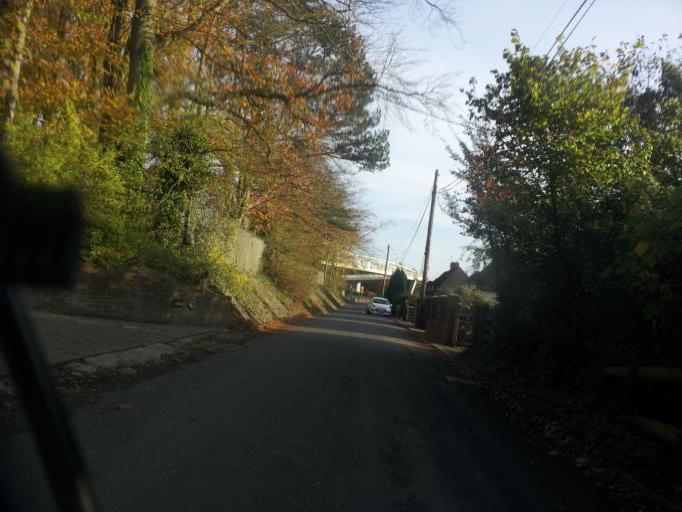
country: GB
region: England
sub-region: Kent
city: Boxley
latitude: 51.2973
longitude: 0.5665
